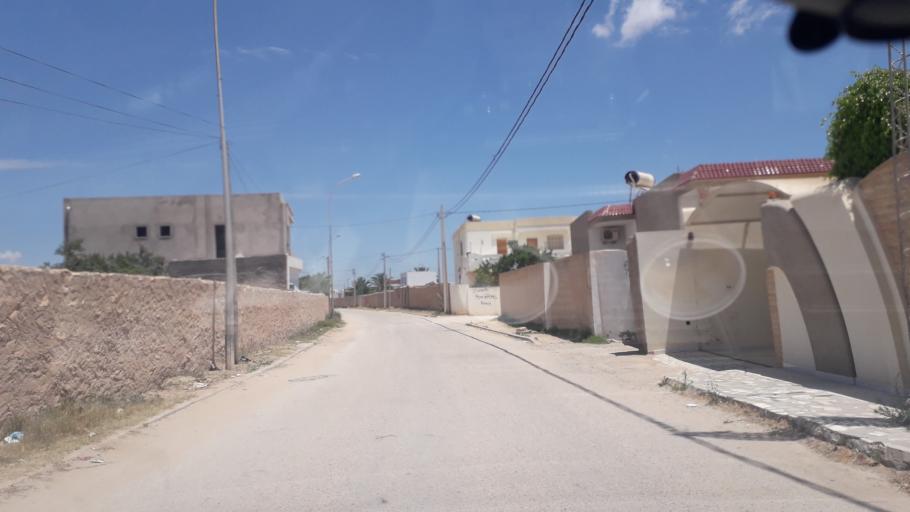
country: TN
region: Safaqis
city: Al Qarmadah
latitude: 34.8160
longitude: 10.7678
